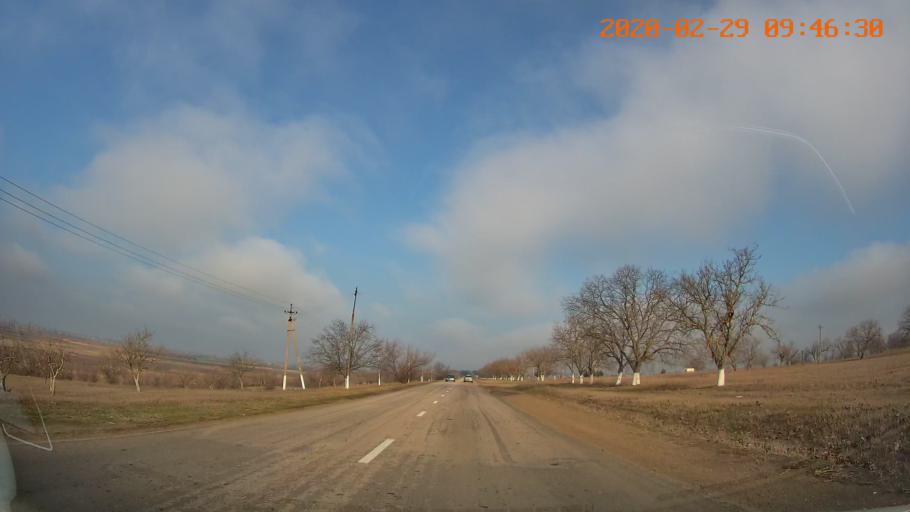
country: MD
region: Telenesti
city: Crasnoe
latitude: 46.6676
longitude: 29.7980
